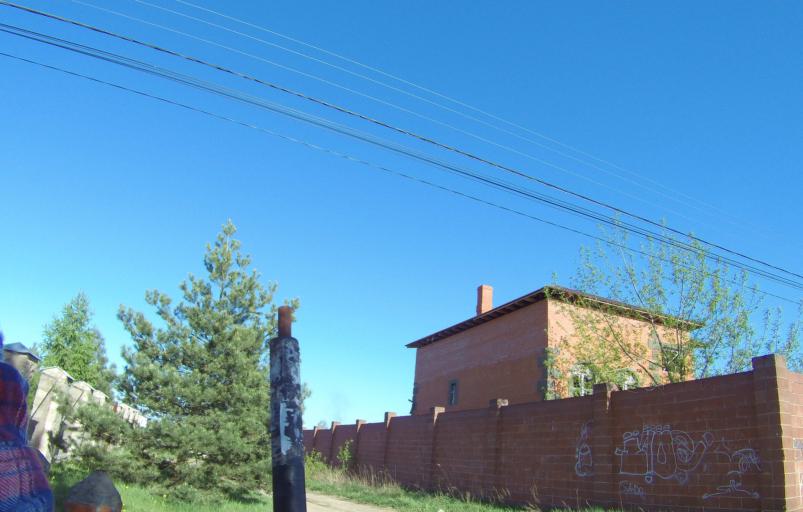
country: RU
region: Moskovskaya
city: Ramenskoye
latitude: 55.5487
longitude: 38.1933
